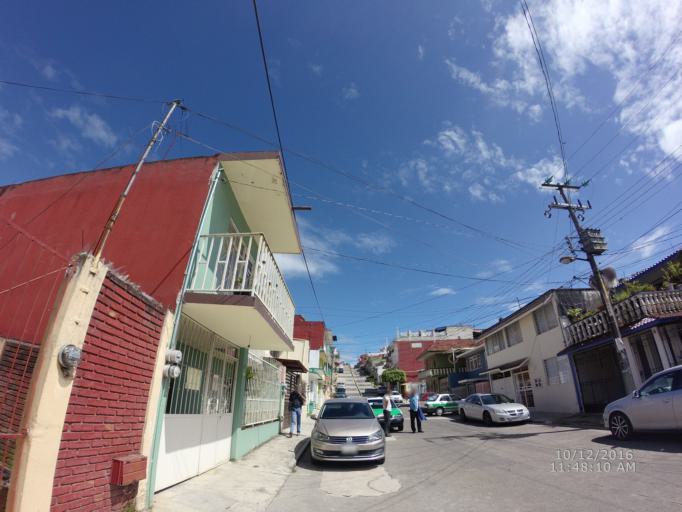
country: MX
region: Veracruz
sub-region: Tlalnelhuayocan
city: Guadalupe Victoria
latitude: 19.5551
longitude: -96.9343
